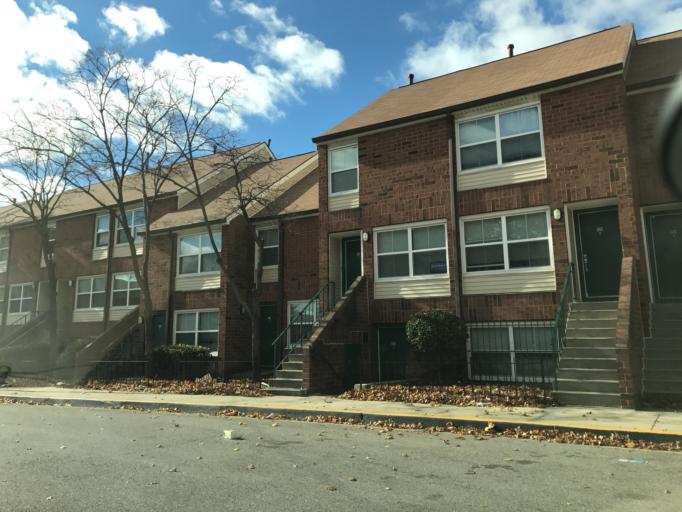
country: US
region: Maryland
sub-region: City of Baltimore
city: Baltimore
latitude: 39.2788
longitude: -76.6176
